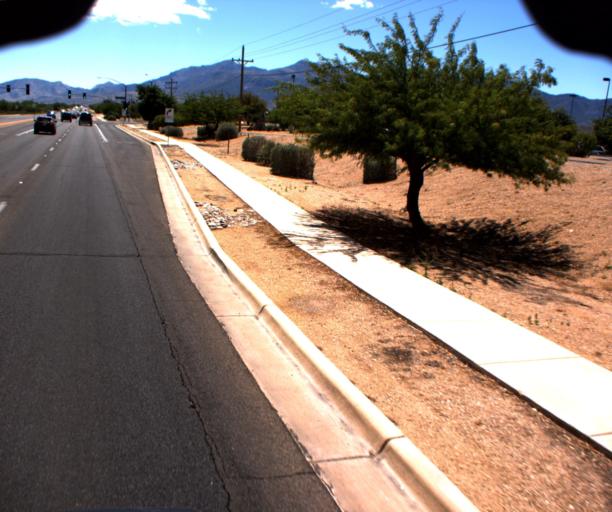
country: US
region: Arizona
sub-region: Cochise County
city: Sierra Vista
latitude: 31.5298
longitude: -110.2574
